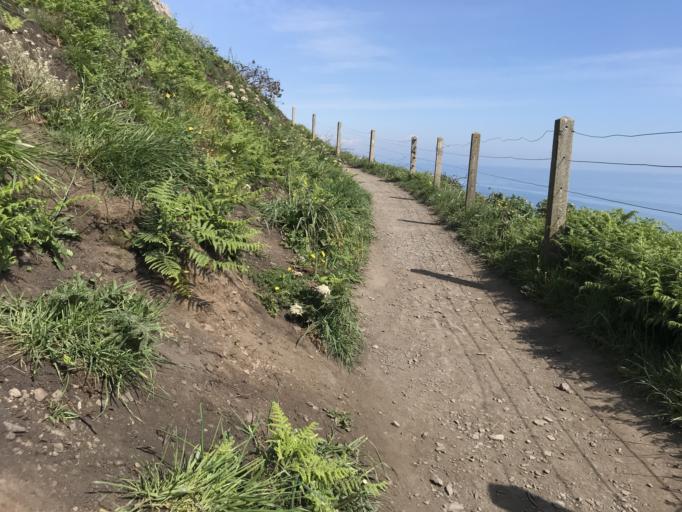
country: IE
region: Leinster
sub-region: Wicklow
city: Bray
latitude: 53.1807
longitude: -6.0758
